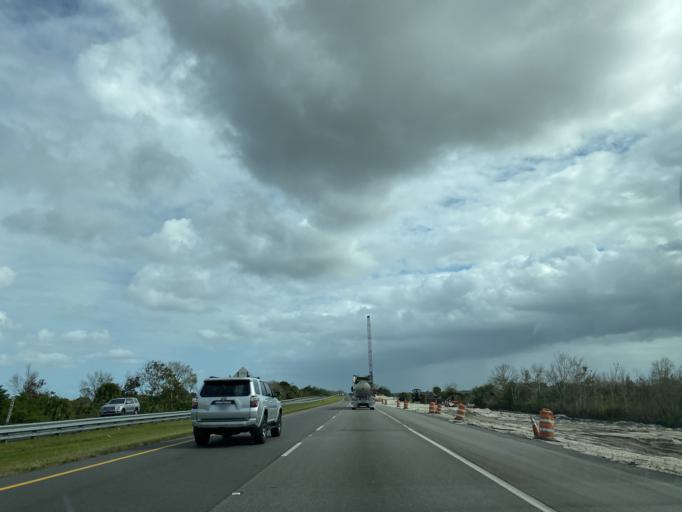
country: US
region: Florida
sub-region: Brevard County
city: Port Saint John
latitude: 28.4525
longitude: -80.9078
